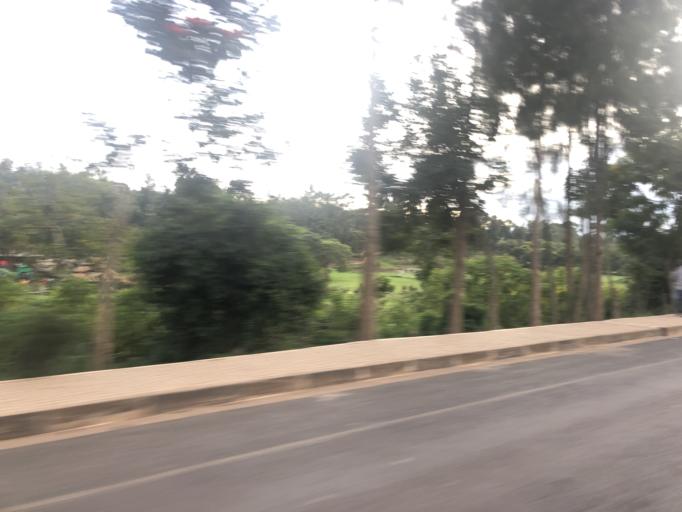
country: RW
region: Kigali
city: Kigali
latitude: -1.9301
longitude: 30.0808
